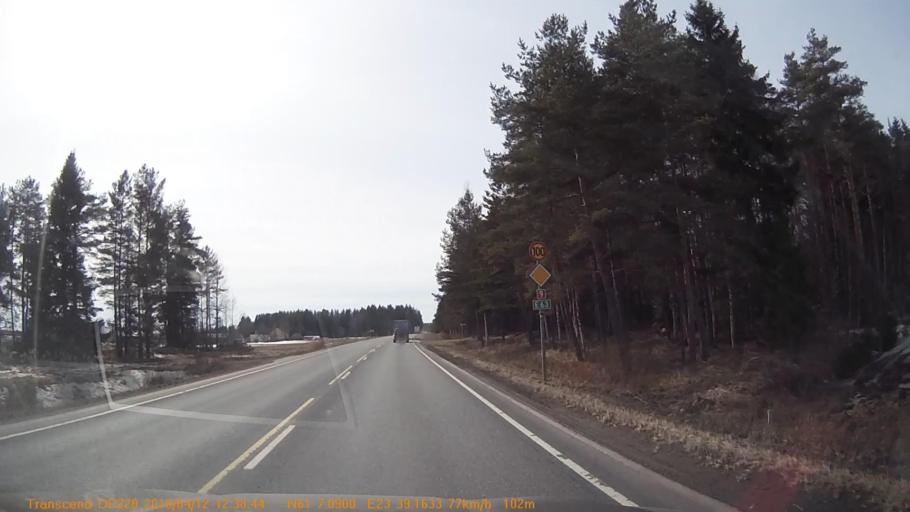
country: FI
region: Pirkanmaa
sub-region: Etelae-Pirkanmaa
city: Kylmaekoski
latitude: 61.1183
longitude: 23.6530
